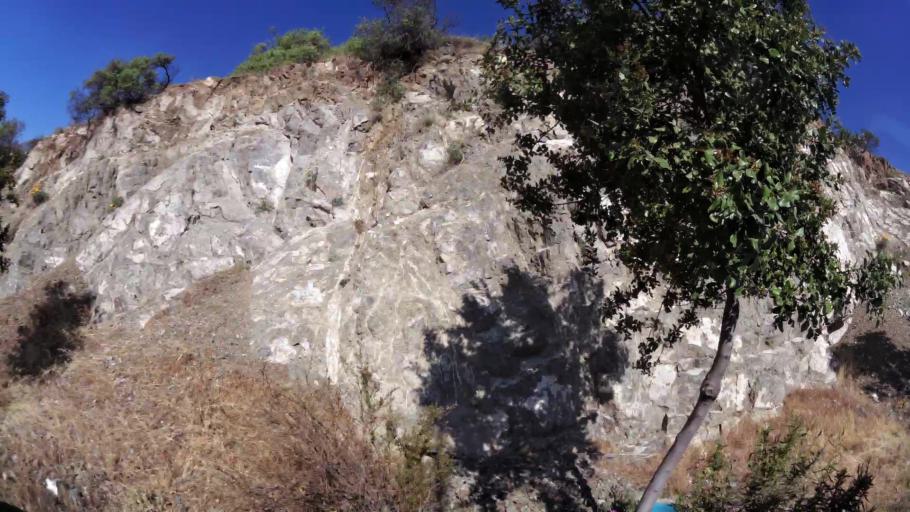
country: CL
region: Santiago Metropolitan
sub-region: Provincia de Santiago
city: Villa Presidente Frei, Nunoa, Santiago, Chile
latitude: -33.3702
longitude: -70.4947
